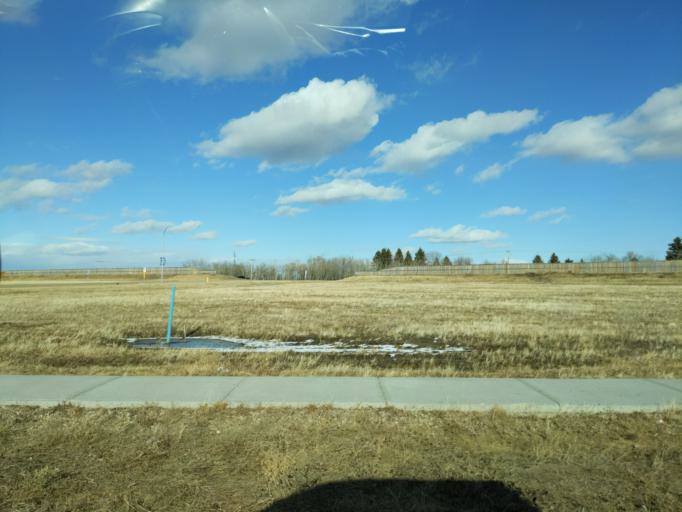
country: CA
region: Saskatchewan
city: Lloydminster
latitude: 53.2661
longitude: -109.9810
